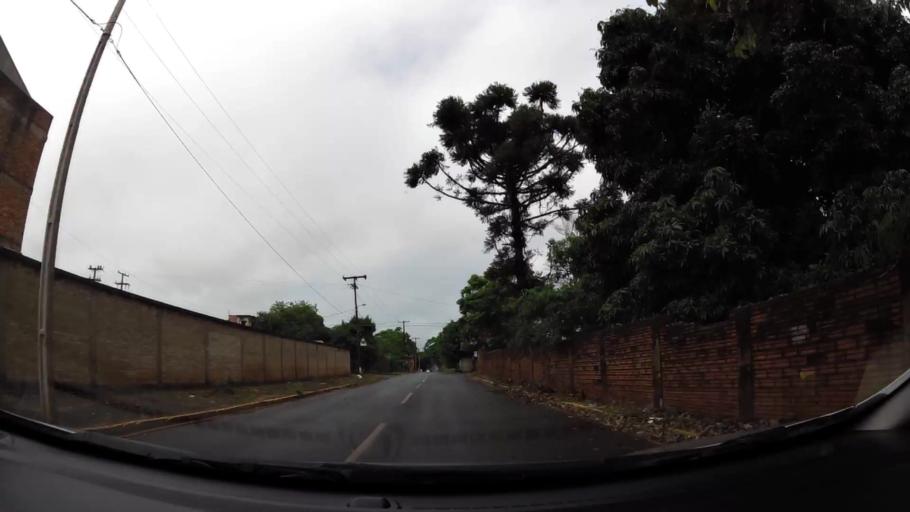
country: PY
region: Alto Parana
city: Ciudad del Este
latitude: -25.5068
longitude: -54.6466
